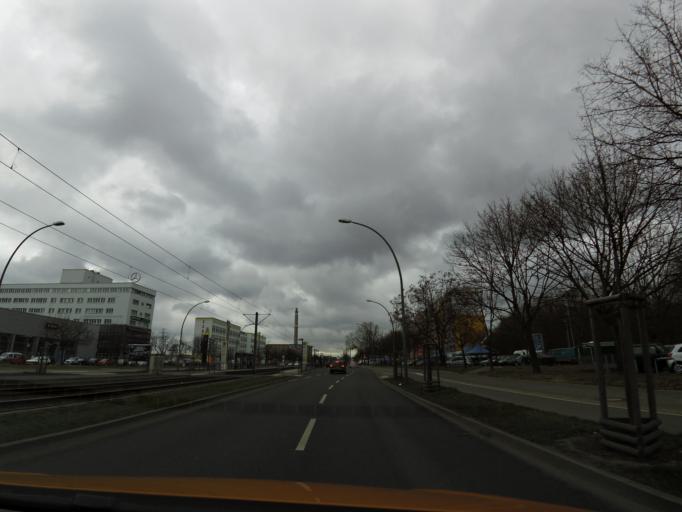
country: DE
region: Berlin
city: Alt-Hohenschoenhausen
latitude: 52.5299
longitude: 13.5191
